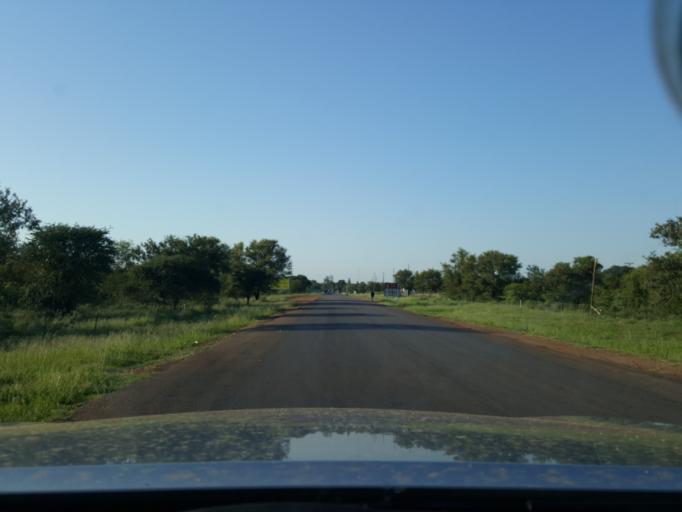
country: BW
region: South East
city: Janeng
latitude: -25.6329
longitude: 25.5742
